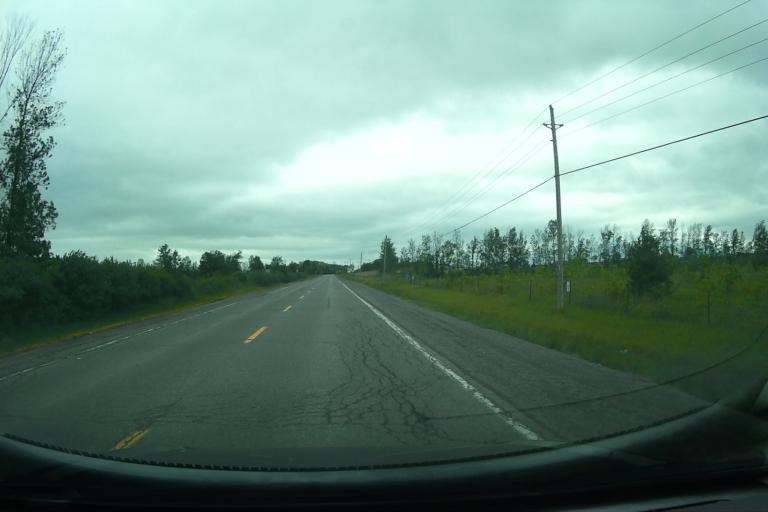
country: CA
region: Ontario
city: Carleton Place
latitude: 45.1251
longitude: -75.9438
